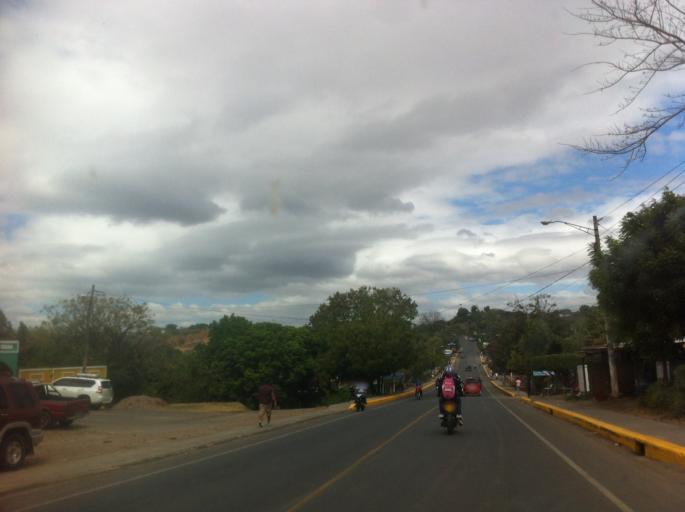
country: NI
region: Chontales
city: Juigalpa
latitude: 12.0990
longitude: -85.3651
